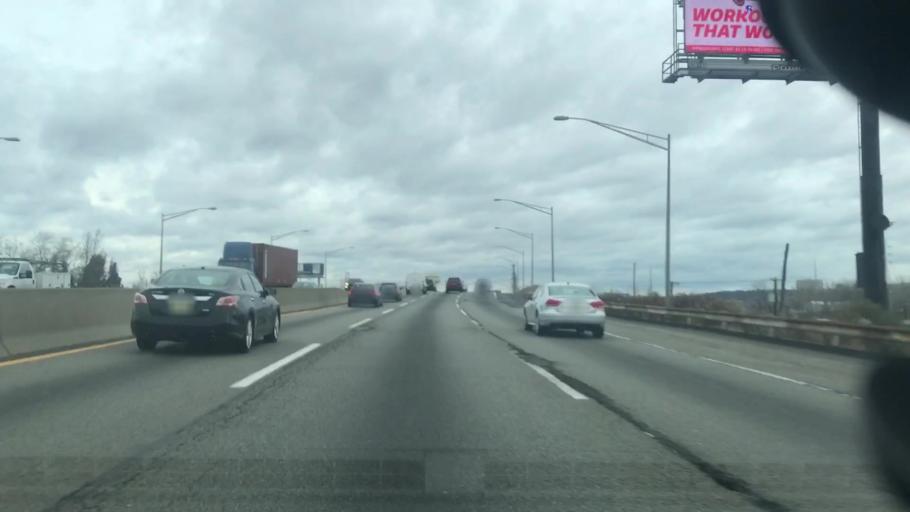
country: US
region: New Jersey
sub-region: Bergen County
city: Ridgefield
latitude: 40.8279
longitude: -74.0256
